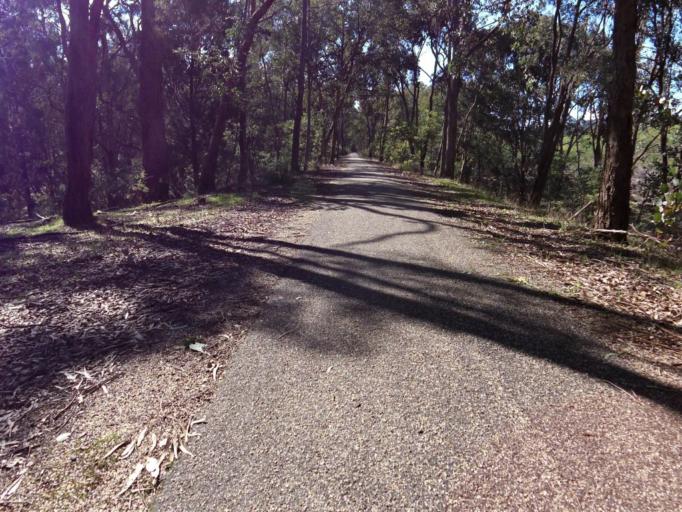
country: AU
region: Victoria
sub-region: Wangaratta
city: Wangaratta
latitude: -36.4040
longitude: 146.6314
